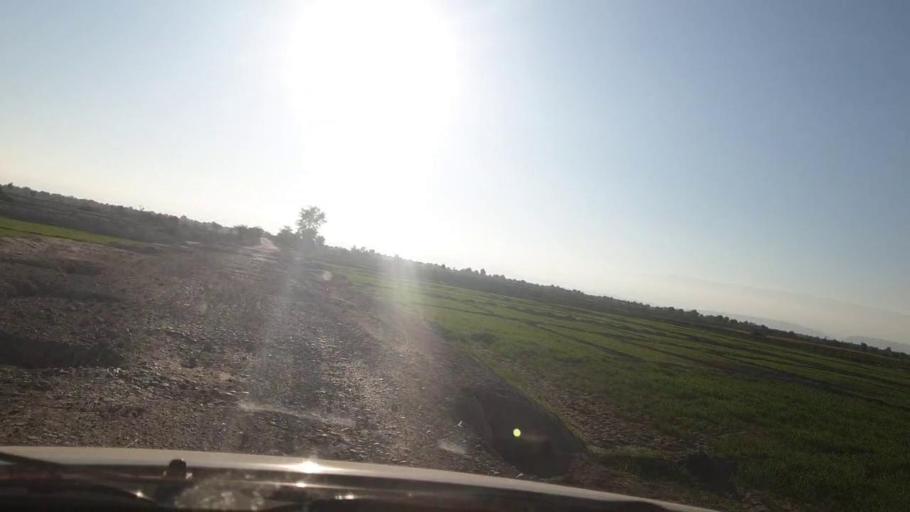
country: PK
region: Sindh
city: Johi
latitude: 26.7727
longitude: 67.4493
